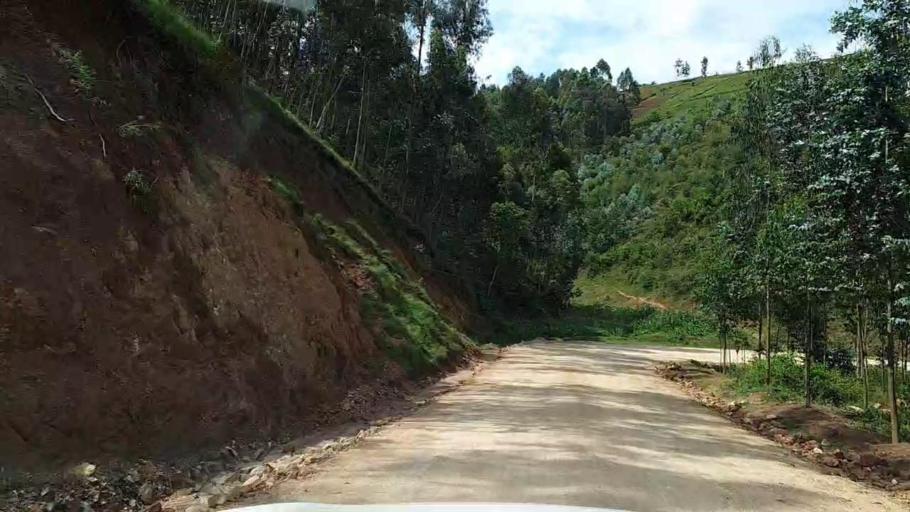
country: RW
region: Southern Province
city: Nzega
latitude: -2.3414
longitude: 29.4366
